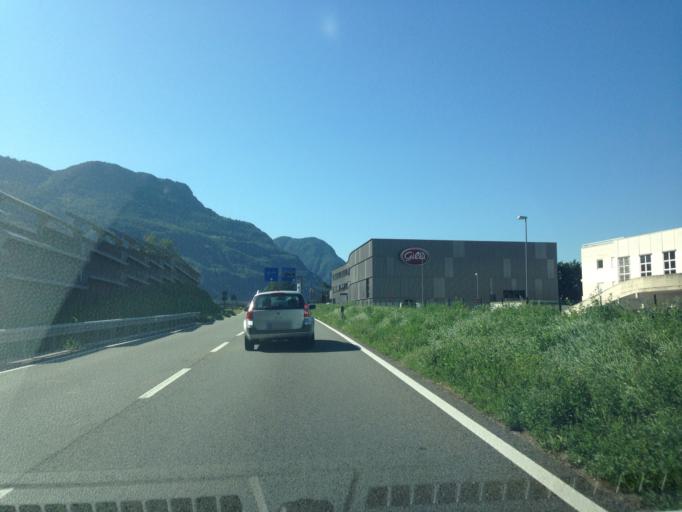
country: IT
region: Trentino-Alto Adige
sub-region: Bolzano
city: Pineta
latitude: 46.4464
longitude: 11.3434
